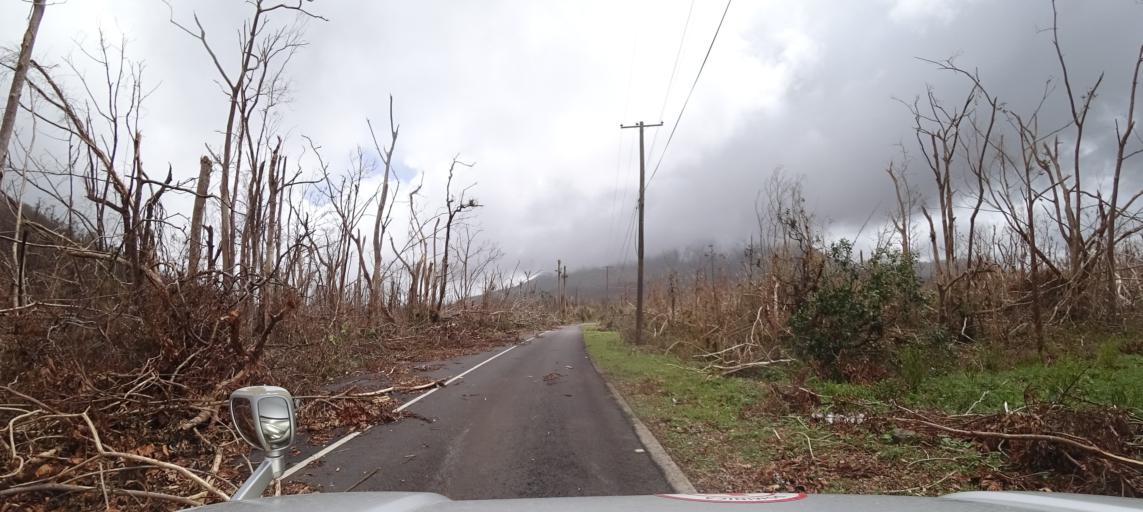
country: DM
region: Saint Paul
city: Pont Casse
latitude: 15.4053
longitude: -61.3424
